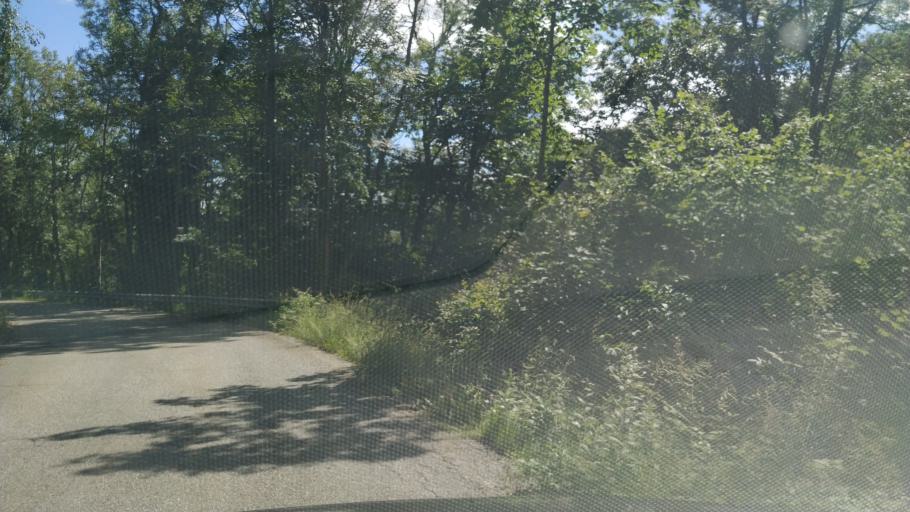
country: IT
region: Piedmont
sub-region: Provincia di Torino
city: Castelnuovo Nigra
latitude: 45.4367
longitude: 7.7007
